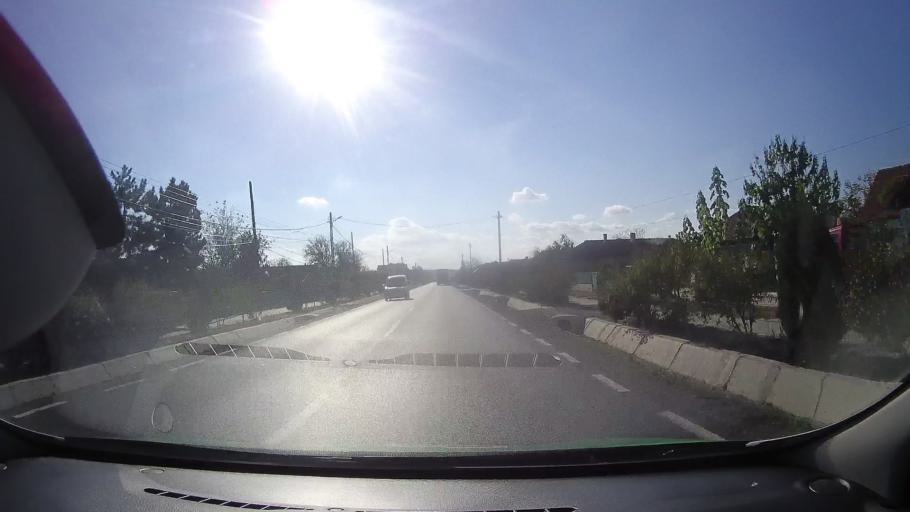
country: RO
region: Tulcea
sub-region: Comuna Baia
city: Baia
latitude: 44.7293
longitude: 28.6812
